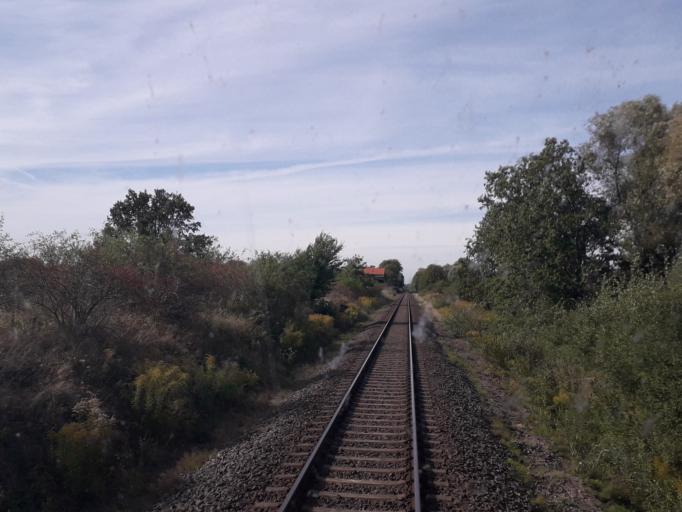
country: DE
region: Brandenburg
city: Velten
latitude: 52.7201
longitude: 13.1190
